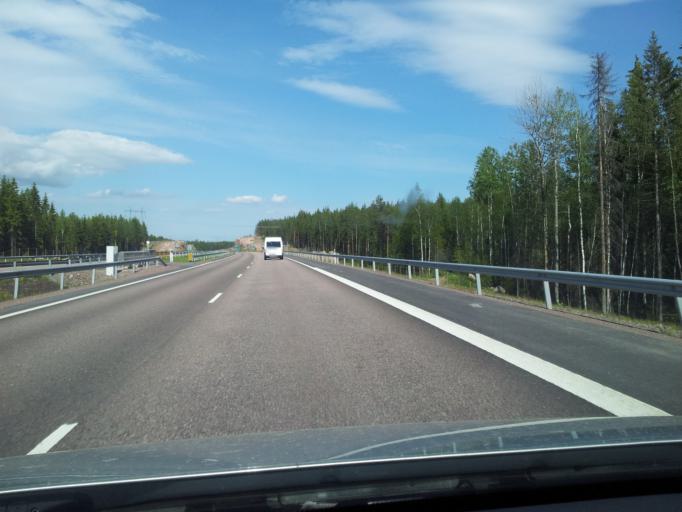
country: FI
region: Uusimaa
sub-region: Loviisa
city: Lovisa
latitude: 60.4778
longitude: 26.2754
